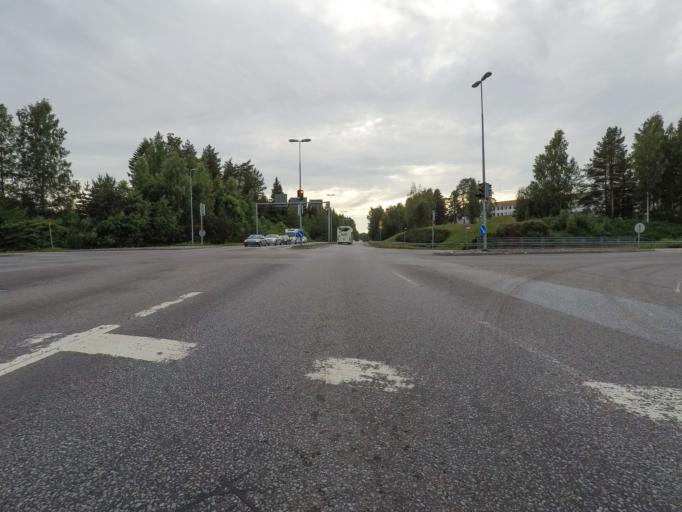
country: FI
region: Southern Savonia
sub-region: Savonlinna
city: Savonlinna
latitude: 61.8670
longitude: 28.9402
